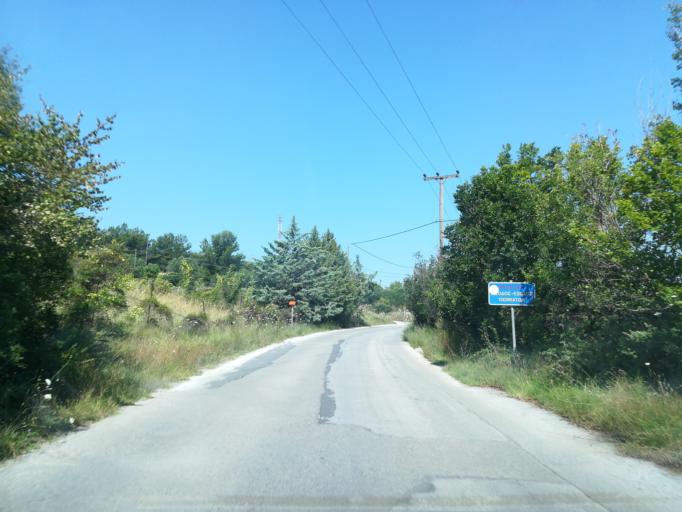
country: GR
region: Central Macedonia
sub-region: Nomos Thessalonikis
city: Asvestochori
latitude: 40.6335
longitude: 23.0244
